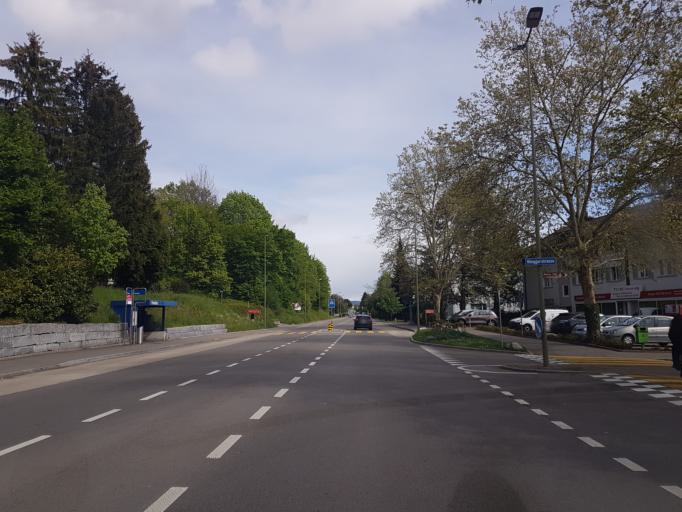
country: CH
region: Zurich
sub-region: Bezirk Dietikon
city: Oberengstringen / Sonnenberg
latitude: 47.4111
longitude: 8.4583
